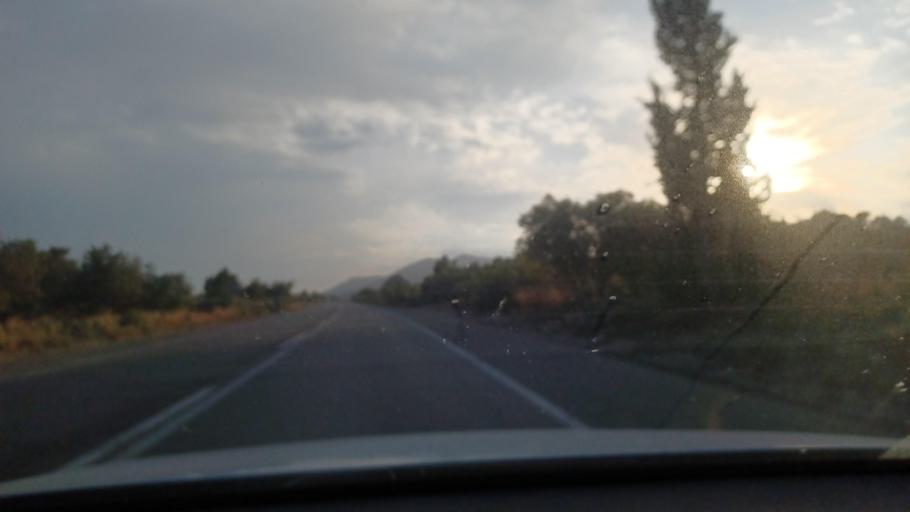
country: ES
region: Catalonia
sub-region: Provincia de Tarragona
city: Colldejou
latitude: 40.9860
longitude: 0.9057
